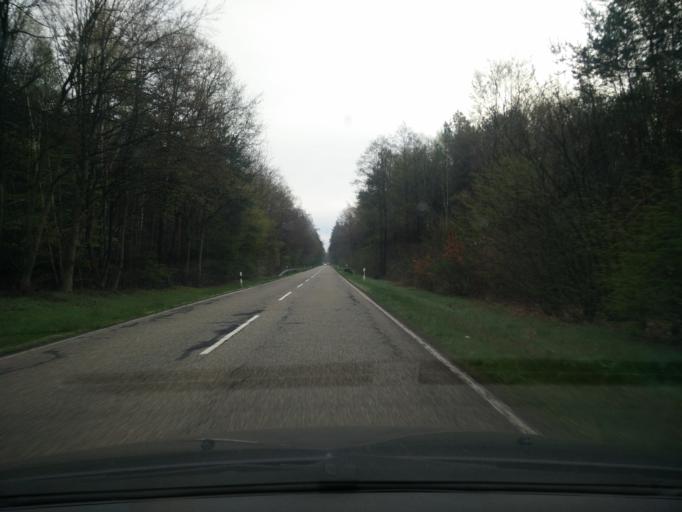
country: DE
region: Rheinland-Pfalz
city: Kandel
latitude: 49.0520
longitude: 8.1848
